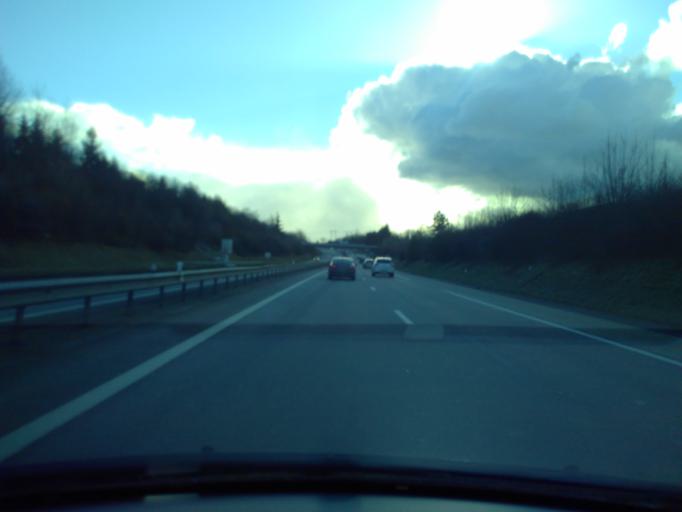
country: FR
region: Rhone-Alpes
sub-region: Departement de la Haute-Savoie
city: Cran-Gevrier
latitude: 45.9036
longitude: 6.0926
